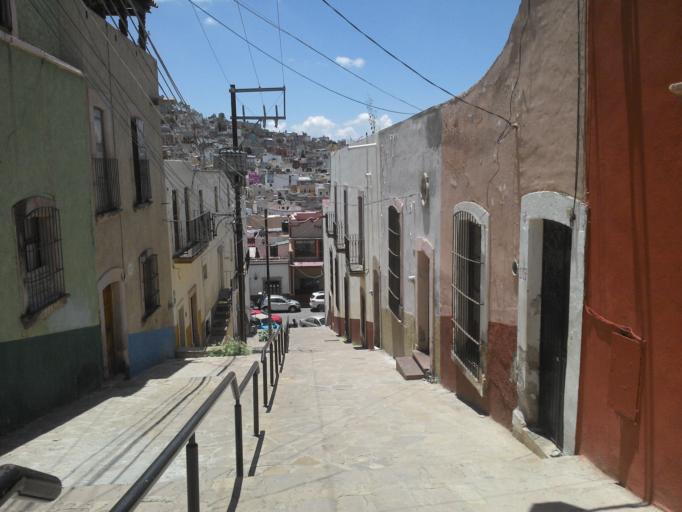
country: MX
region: Zacatecas
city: Zacatecas
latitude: 22.7776
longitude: -102.5728
